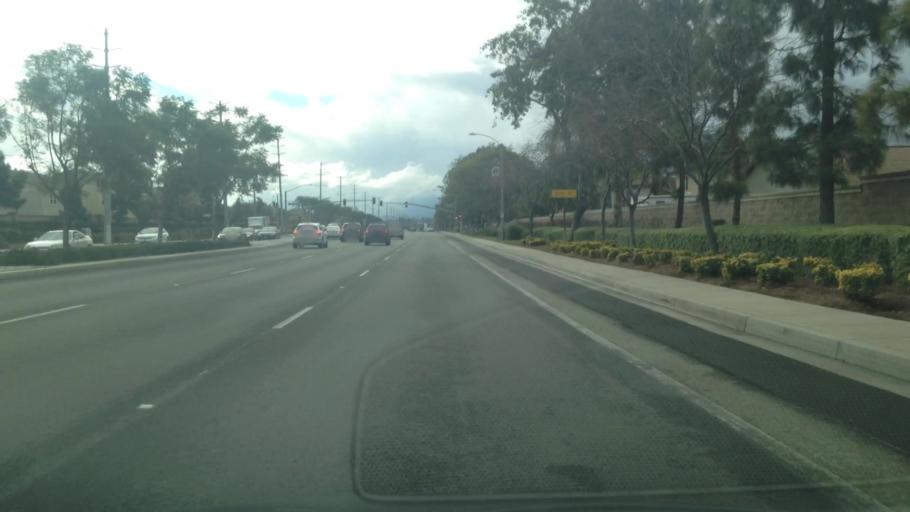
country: US
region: California
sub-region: Riverside County
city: Norco
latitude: 33.9701
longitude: -117.5584
